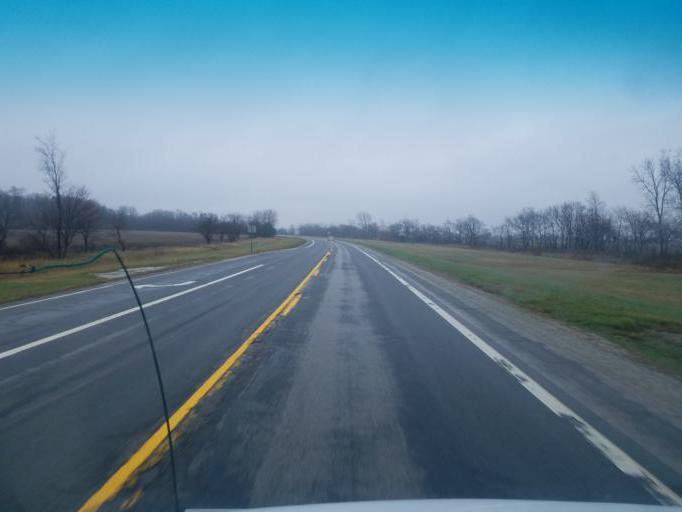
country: US
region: Ohio
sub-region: Wood County
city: Bowling Green
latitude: 41.3536
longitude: -83.6895
